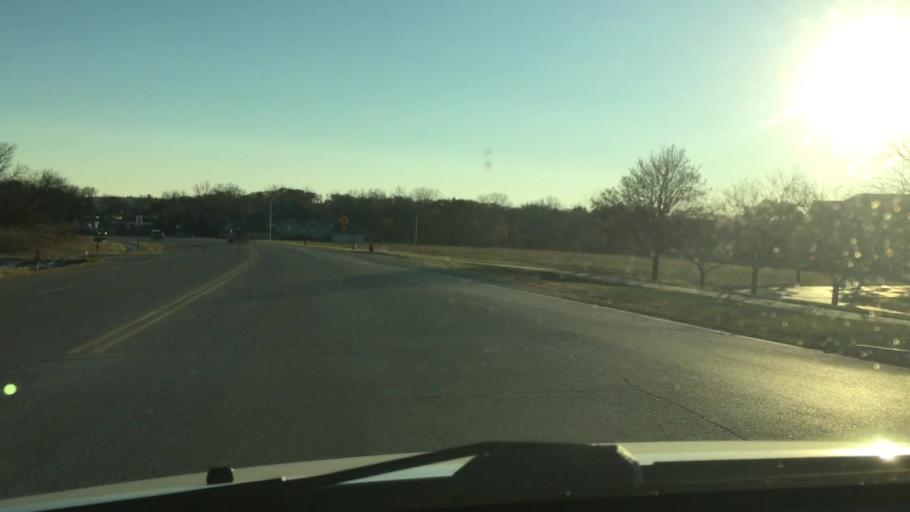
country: US
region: Wisconsin
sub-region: Waukesha County
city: Pewaukee
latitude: 43.0928
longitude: -88.2744
